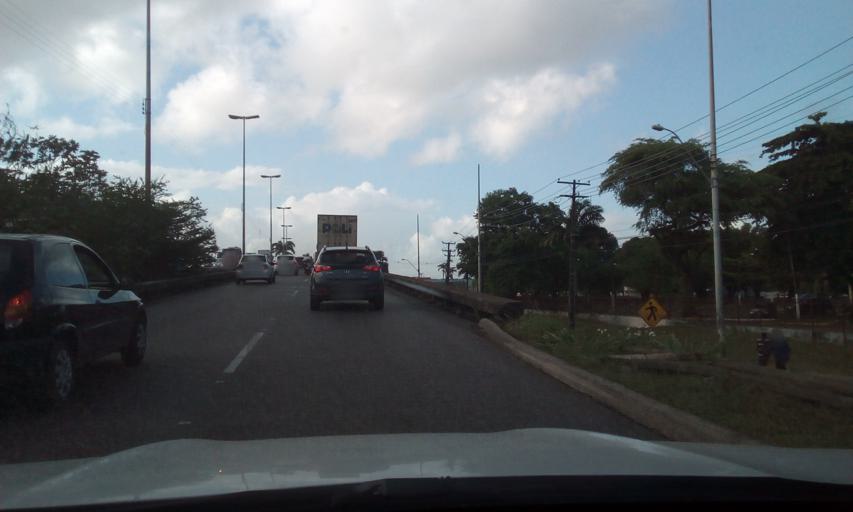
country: BR
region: Pernambuco
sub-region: Recife
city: Recife
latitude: -8.0504
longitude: -34.9459
